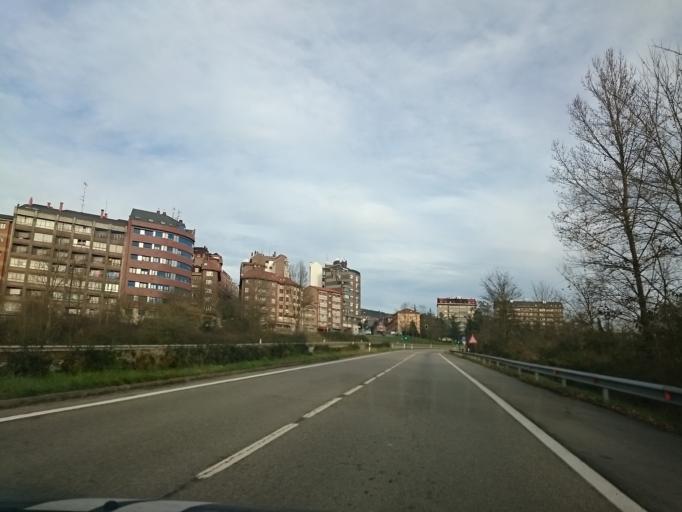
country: ES
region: Asturias
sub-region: Province of Asturias
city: Oviedo
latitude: 43.3522
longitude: -5.8561
